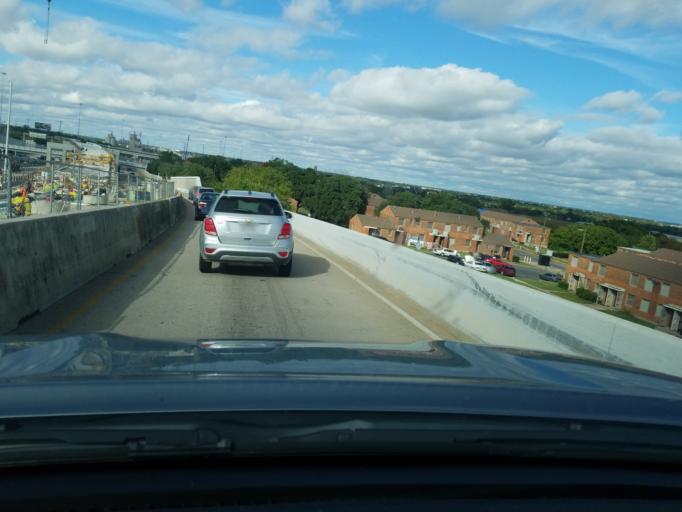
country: US
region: Texas
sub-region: Tarrant County
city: Fort Worth
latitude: 32.7480
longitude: -97.3186
